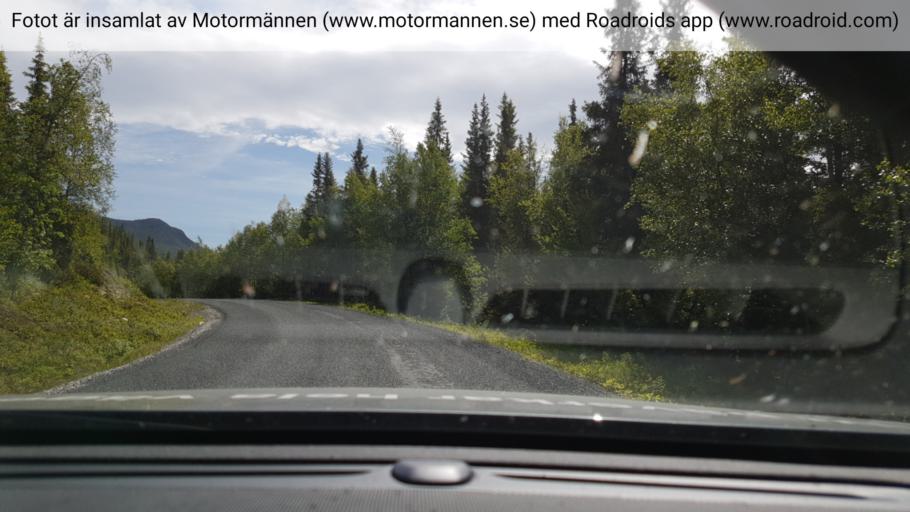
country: SE
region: Vaesterbotten
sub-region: Vilhelmina Kommun
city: Sjoberg
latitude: 65.2622
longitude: 15.3793
